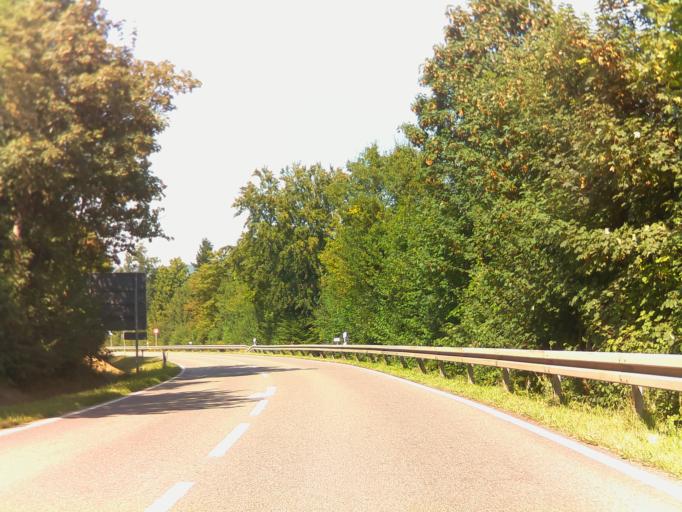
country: DE
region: Baden-Wuerttemberg
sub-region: Karlsruhe Region
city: Bretten
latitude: 49.1017
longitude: 8.7148
